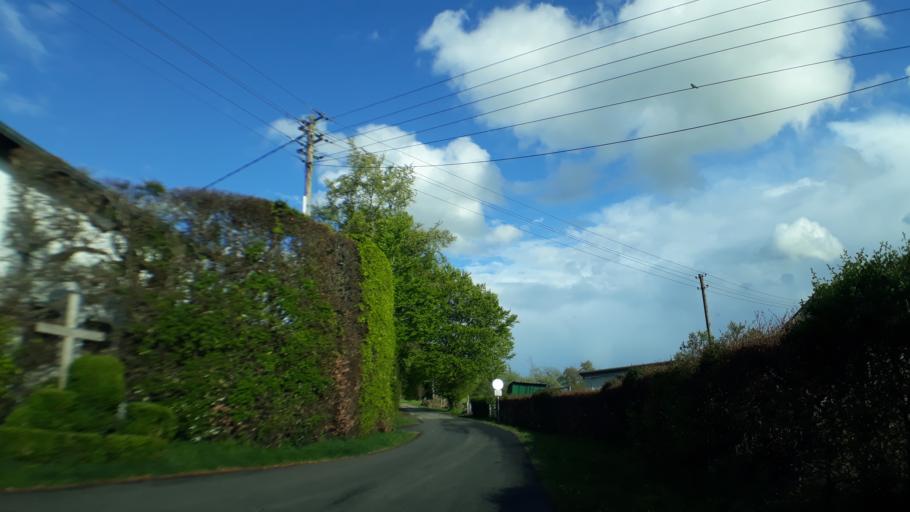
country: DE
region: North Rhine-Westphalia
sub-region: Regierungsbezirk Koln
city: Simmerath
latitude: 50.6184
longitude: 6.2831
